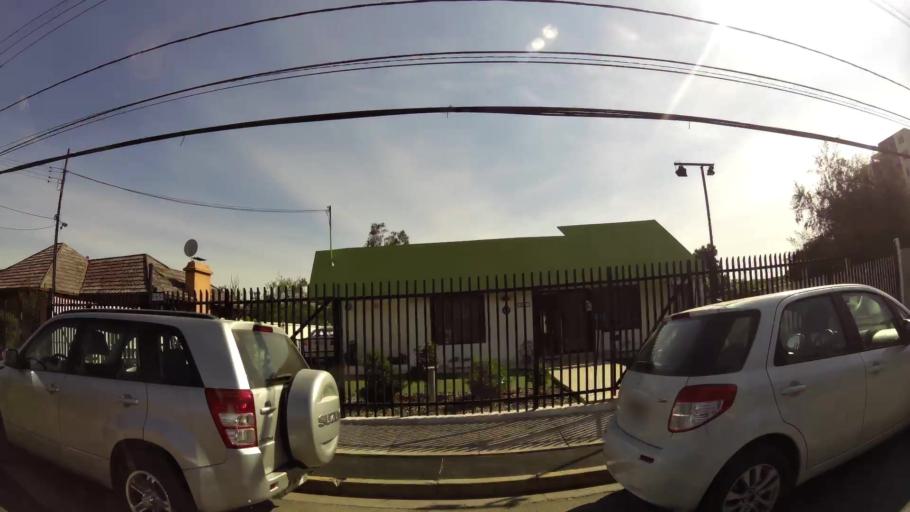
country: CL
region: Santiago Metropolitan
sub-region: Provincia de Santiago
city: La Pintana
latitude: -33.5339
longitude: -70.5923
